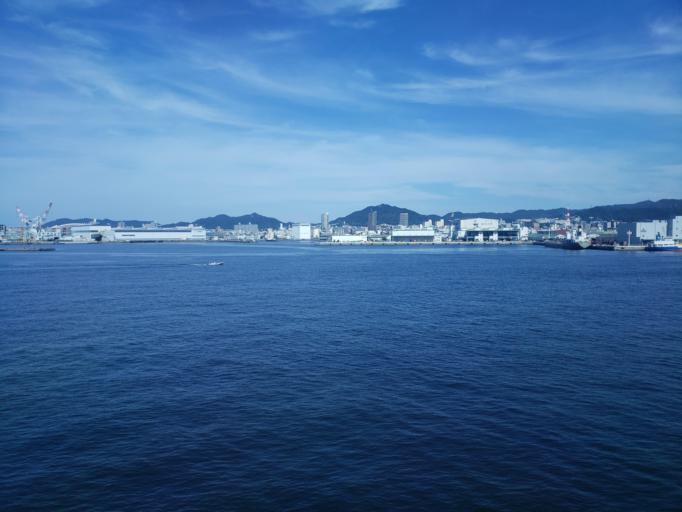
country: JP
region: Hyogo
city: Kobe
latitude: 34.6606
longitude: 135.1898
